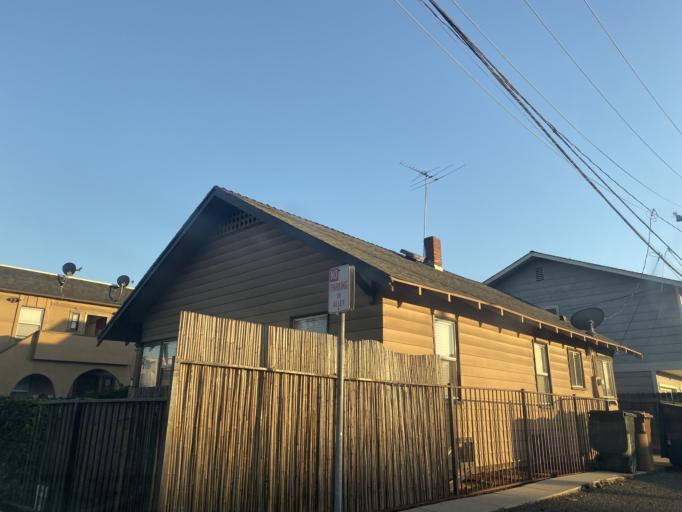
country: US
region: California
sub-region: Orange County
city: Fullerton
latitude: 33.8749
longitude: -117.9228
